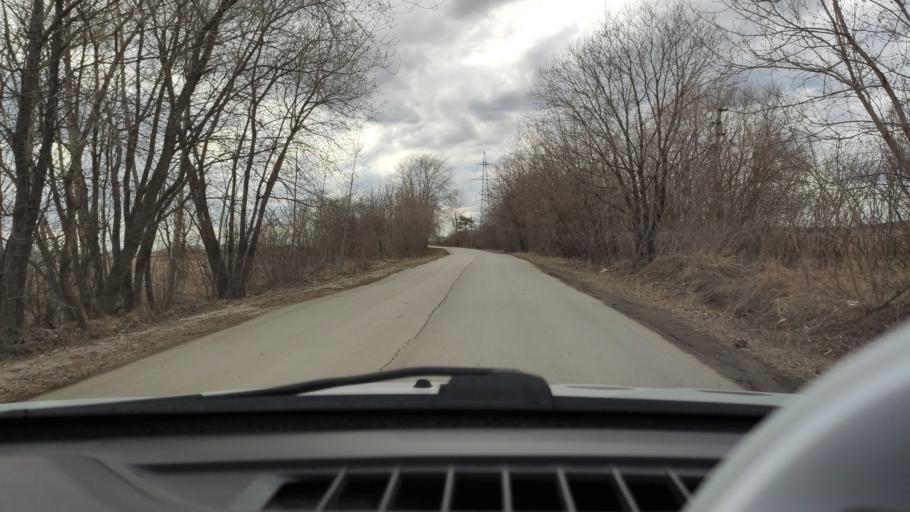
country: RU
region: Perm
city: Froly
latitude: 57.9292
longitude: 56.2567
